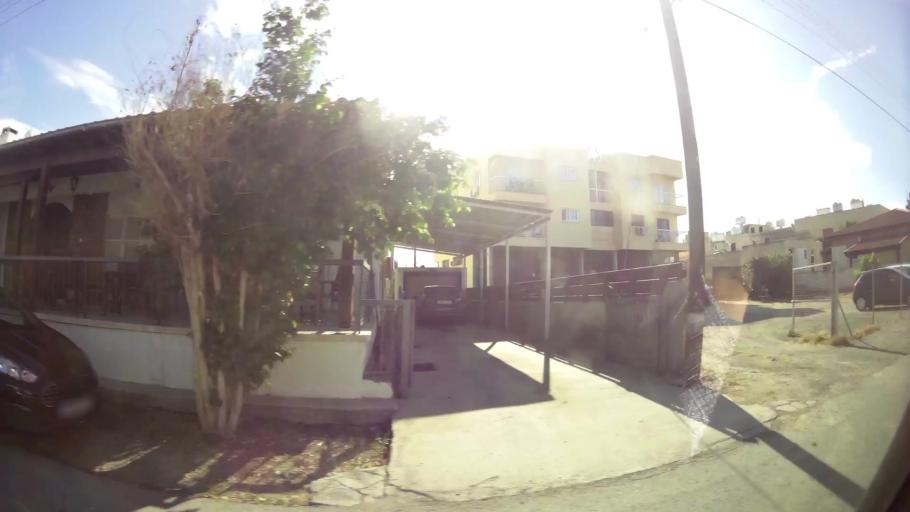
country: CY
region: Lefkosia
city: Nicosia
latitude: 35.1335
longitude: 33.3492
